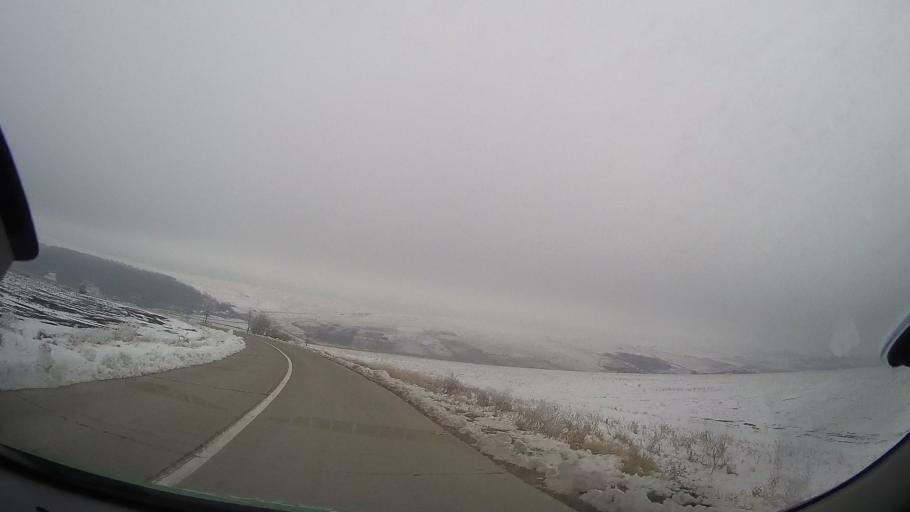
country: RO
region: Vaslui
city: Coroiesti
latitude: 46.2104
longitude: 27.4836
